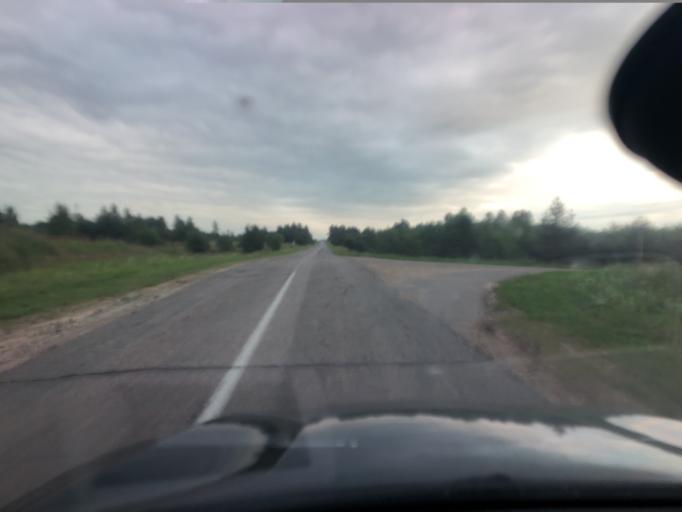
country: RU
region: Jaroslavl
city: Petrovsk
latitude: 57.0083
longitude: 39.0101
